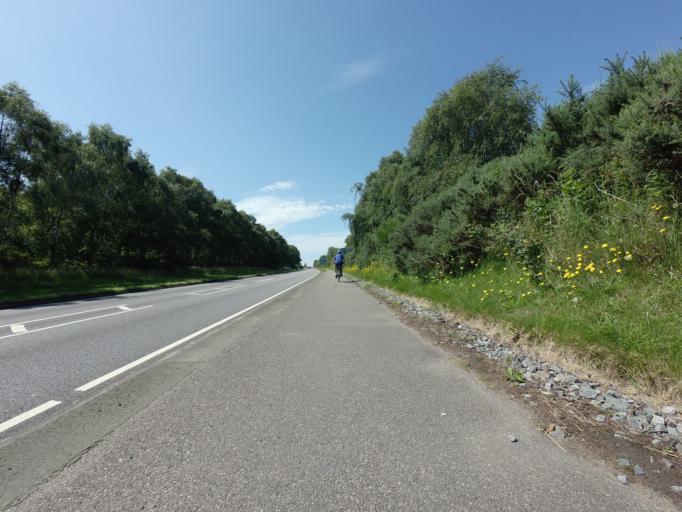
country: GB
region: Scotland
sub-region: Highland
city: Conon Bridge
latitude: 57.5402
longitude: -4.3468
